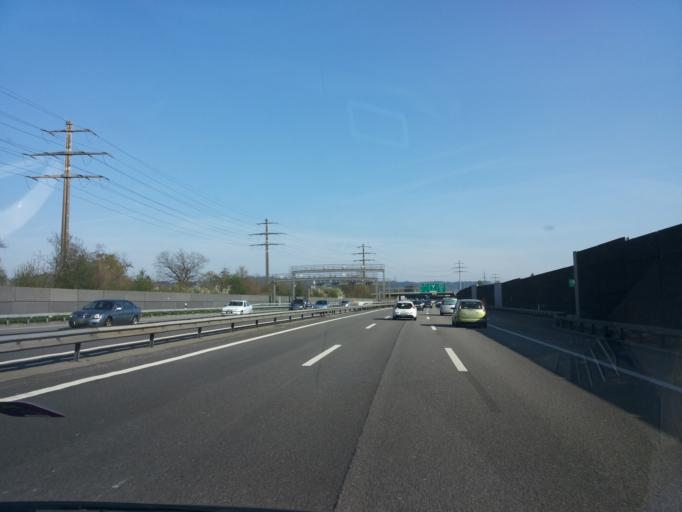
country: CH
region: Aargau
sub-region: Bezirk Zofingen
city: Aarburg
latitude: 47.3095
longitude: 7.9041
